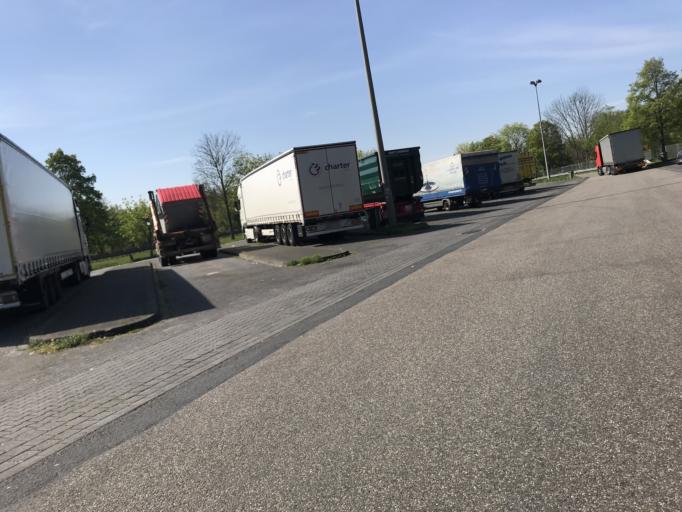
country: DE
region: Hesse
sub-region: Regierungsbezirk Darmstadt
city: Eltville
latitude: 50.0020
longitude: 8.1083
